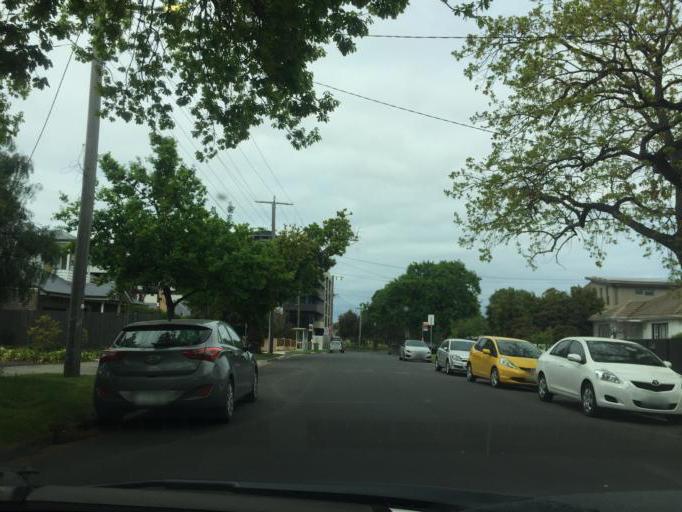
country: AU
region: Victoria
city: Spotswood
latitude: -37.8198
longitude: 144.8868
